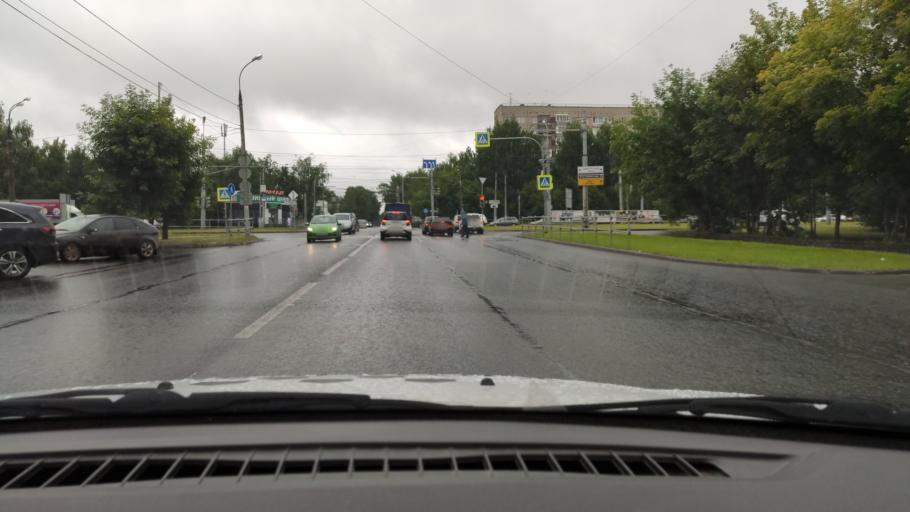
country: RU
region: Udmurtiya
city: Izhevsk
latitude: 56.8759
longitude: 53.2209
